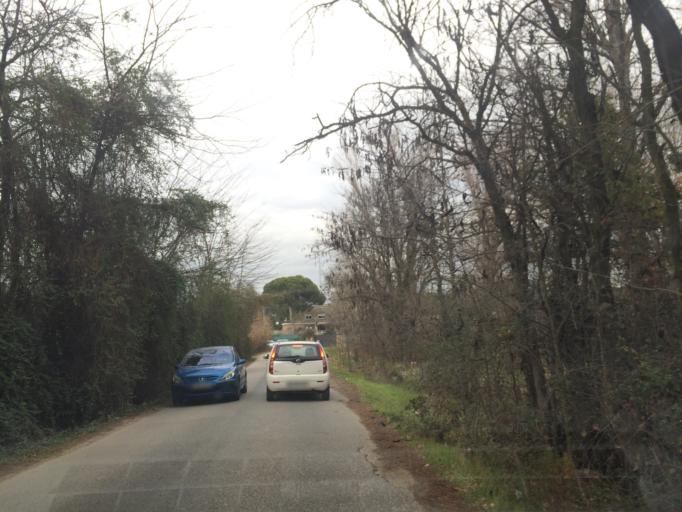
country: ES
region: Madrid
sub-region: Provincia de Madrid
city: Arroyomolinos
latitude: 40.3000
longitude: -3.9440
